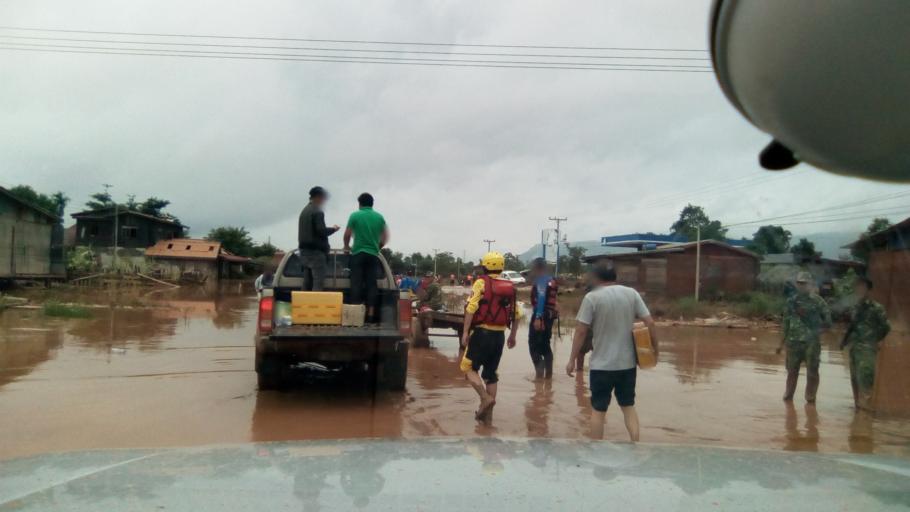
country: LA
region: Attapu
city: Attapu
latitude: 14.7011
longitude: 106.5293
